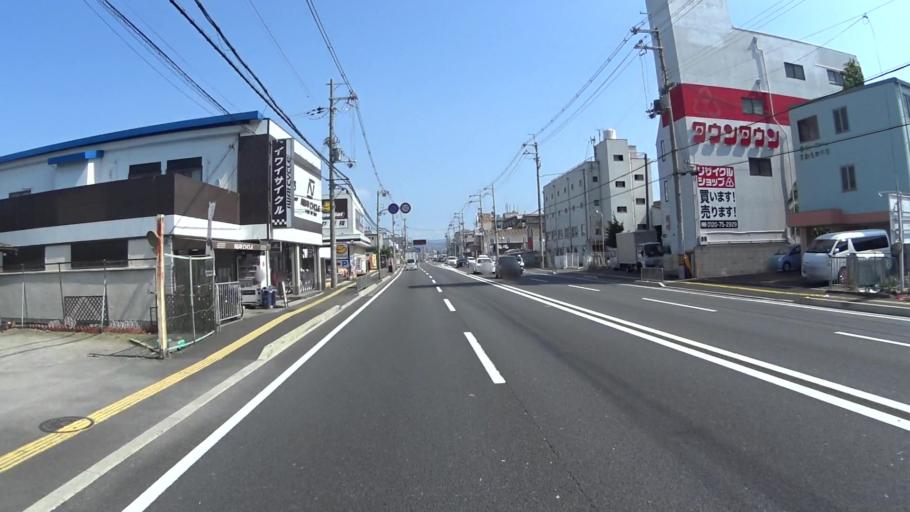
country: JP
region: Kyoto
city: Muko
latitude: 34.9563
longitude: 135.7153
